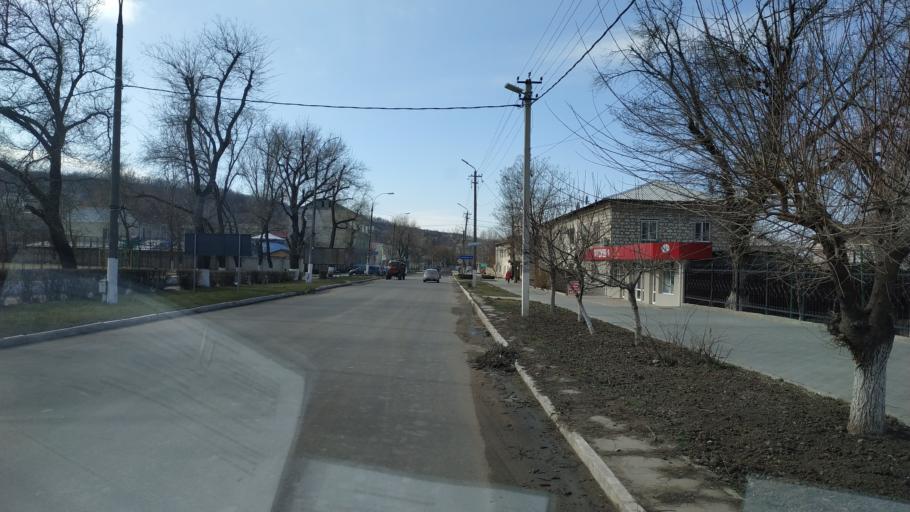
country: MD
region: Causeni
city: Causeni
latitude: 46.6402
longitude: 29.4055
